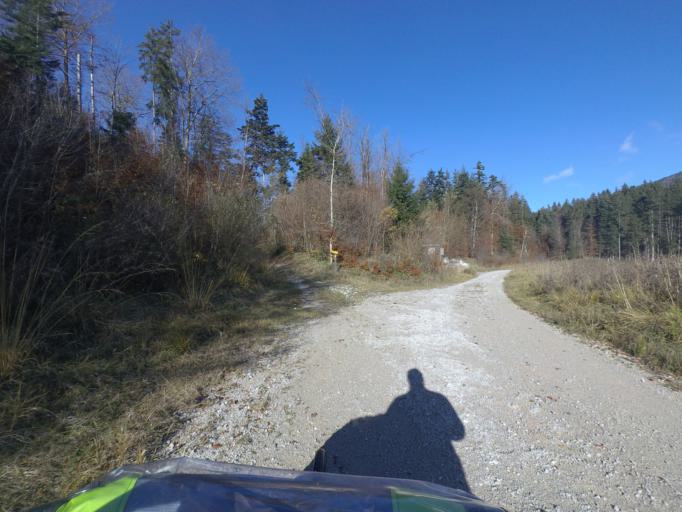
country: AT
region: Salzburg
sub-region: Politischer Bezirk Hallein
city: Adnet
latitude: 47.6810
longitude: 13.1537
